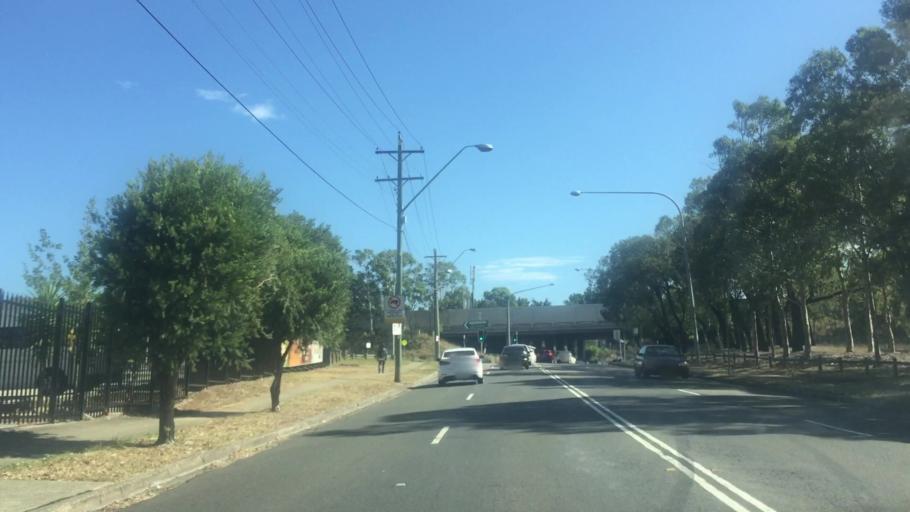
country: AU
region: New South Wales
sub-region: Holroyd
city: Merrylands
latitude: -33.8231
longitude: 150.9890
